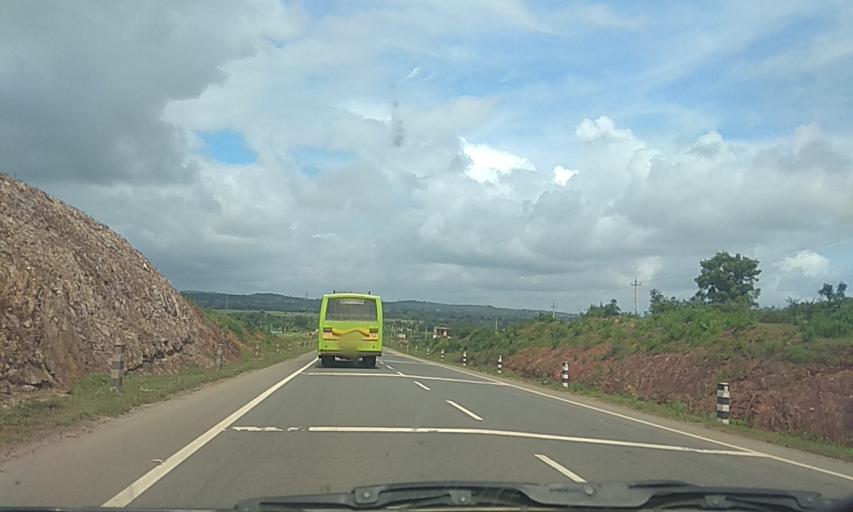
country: IN
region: Karnataka
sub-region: Dharwad
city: Hubli
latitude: 15.4031
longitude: 74.9942
